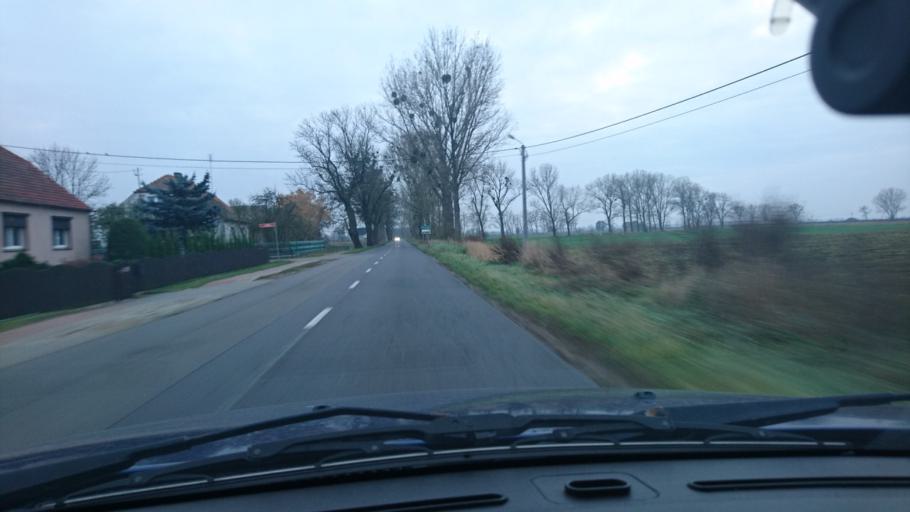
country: PL
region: Greater Poland Voivodeship
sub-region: Powiat ostrowski
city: Odolanow
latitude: 51.5679
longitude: 17.6643
